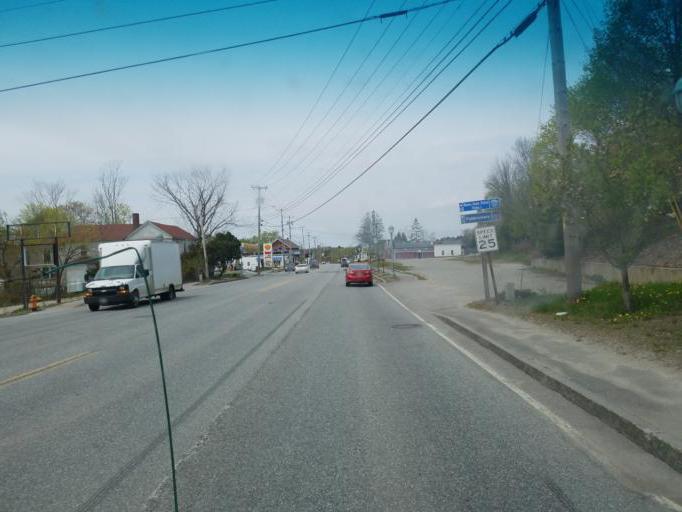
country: US
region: Maine
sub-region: Hancock County
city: Ellsworth
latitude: 44.5401
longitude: -68.4167
